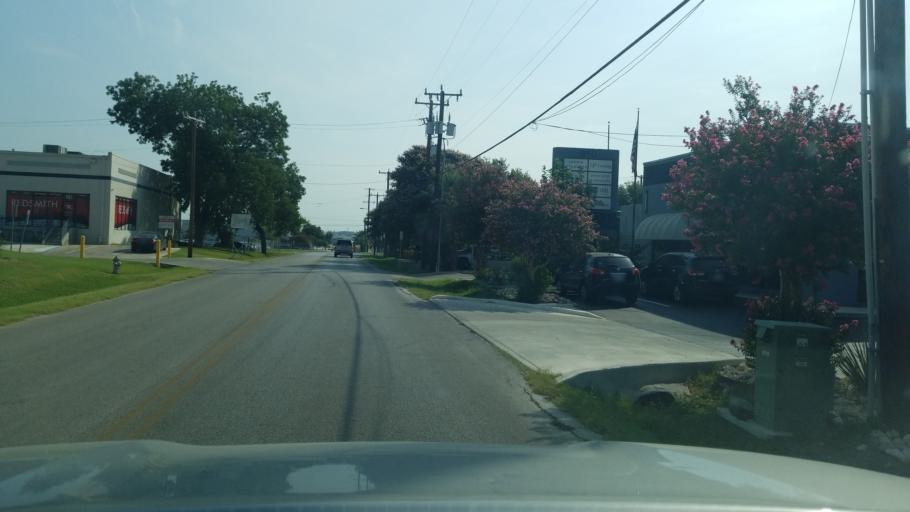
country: US
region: Texas
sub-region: Bexar County
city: Castle Hills
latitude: 29.5355
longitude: -98.4855
